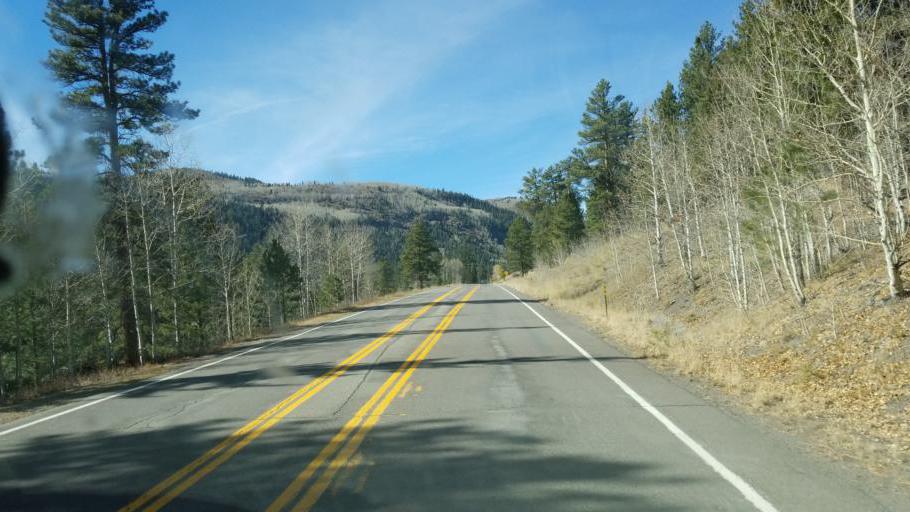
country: US
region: Colorado
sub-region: Conejos County
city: Conejos
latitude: 37.0805
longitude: -106.2963
